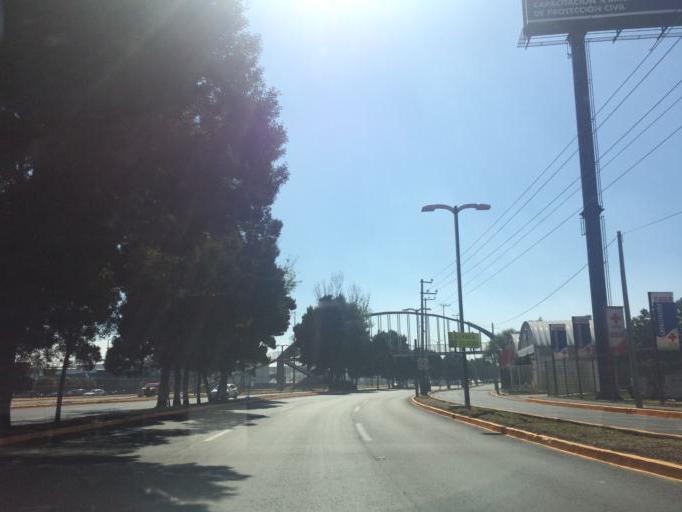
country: MX
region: Mexico
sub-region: Toluca
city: Guadalupe Totoltepec
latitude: 19.3331
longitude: -99.5708
